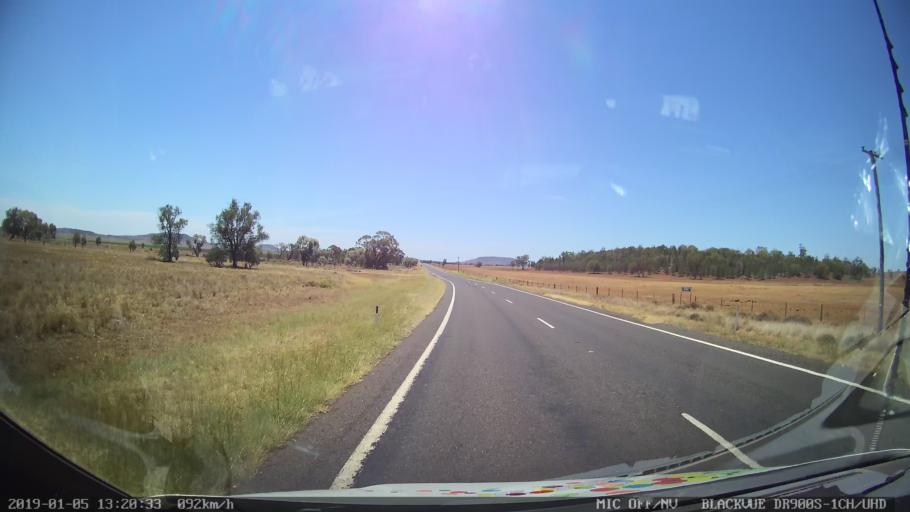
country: AU
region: New South Wales
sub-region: Gunnedah
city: Gunnedah
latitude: -31.1016
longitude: 149.9371
